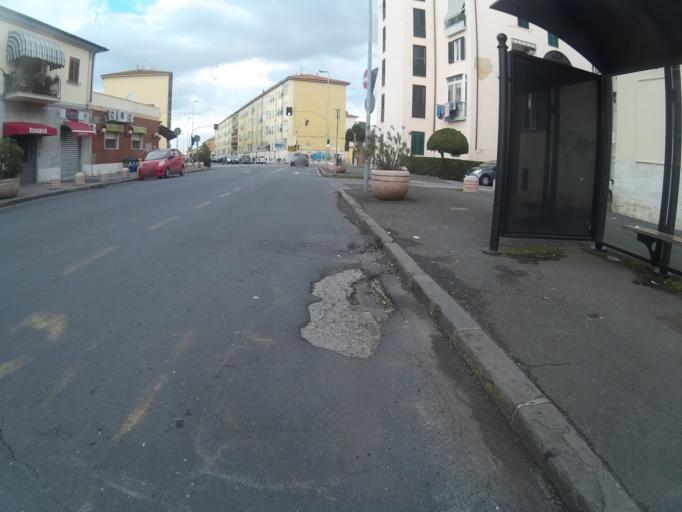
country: IT
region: Tuscany
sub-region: Provincia di Livorno
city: Livorno
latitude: 43.5598
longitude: 10.3324
